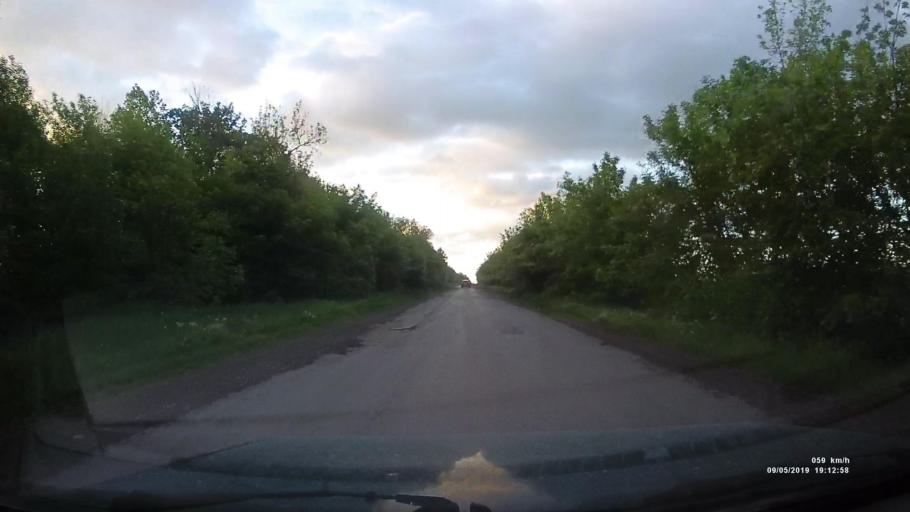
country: RU
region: Krasnodarskiy
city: Kanelovskaya
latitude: 46.7465
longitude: 39.2137
